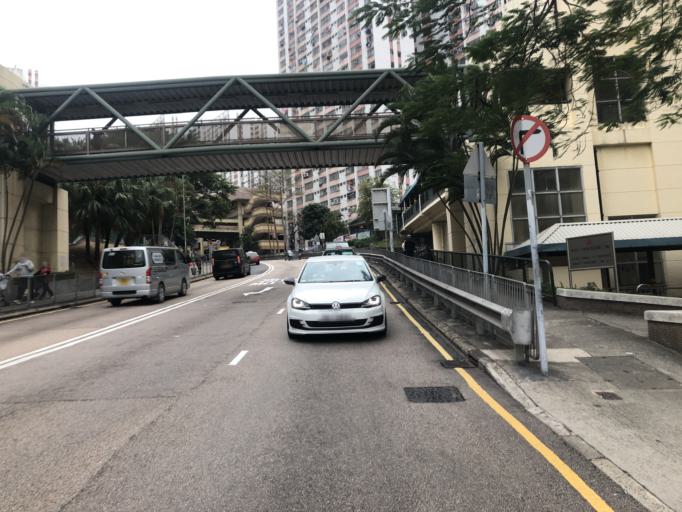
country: HK
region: Wong Tai Sin
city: Wong Tai Sin
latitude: 22.3337
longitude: 114.2134
